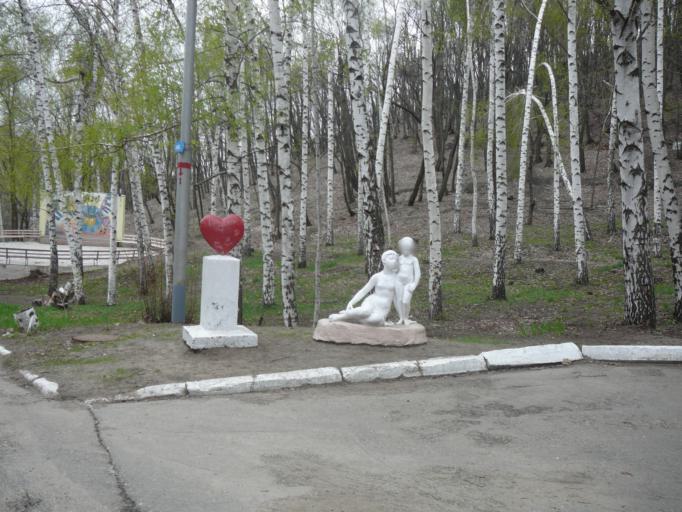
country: RU
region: Saratov
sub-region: Saratovskiy Rayon
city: Saratov
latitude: 51.5487
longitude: 45.9565
